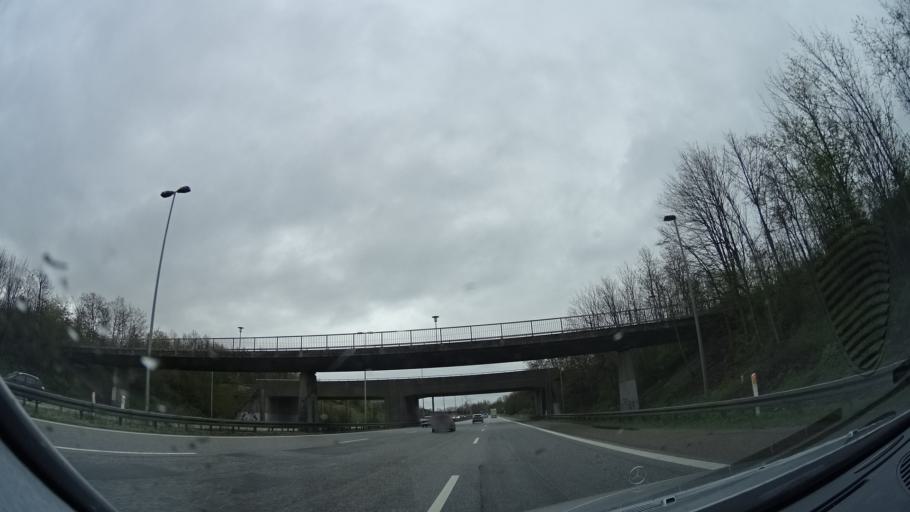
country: DK
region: Capital Region
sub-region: Brondby Kommune
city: Brondbyvester
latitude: 55.6226
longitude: 12.4409
